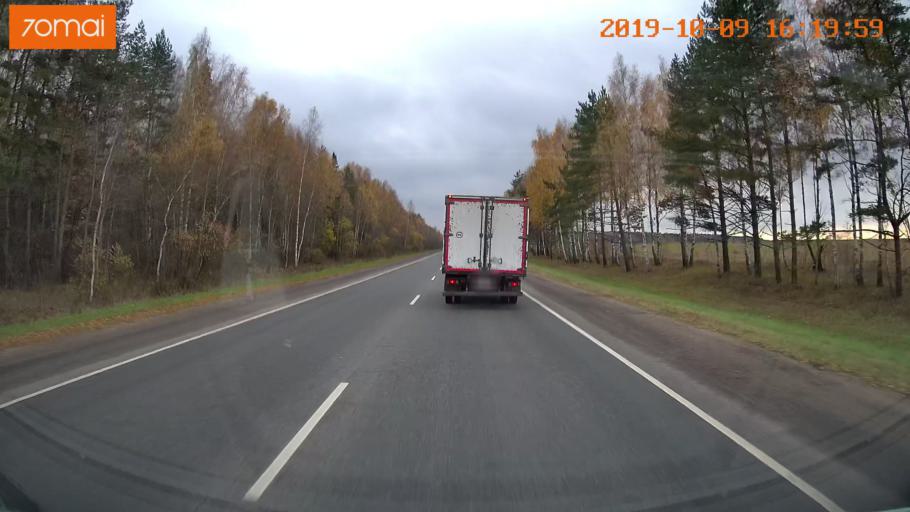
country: RU
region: Kostroma
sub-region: Kostromskoy Rayon
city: Kostroma
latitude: 57.7123
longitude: 40.8934
